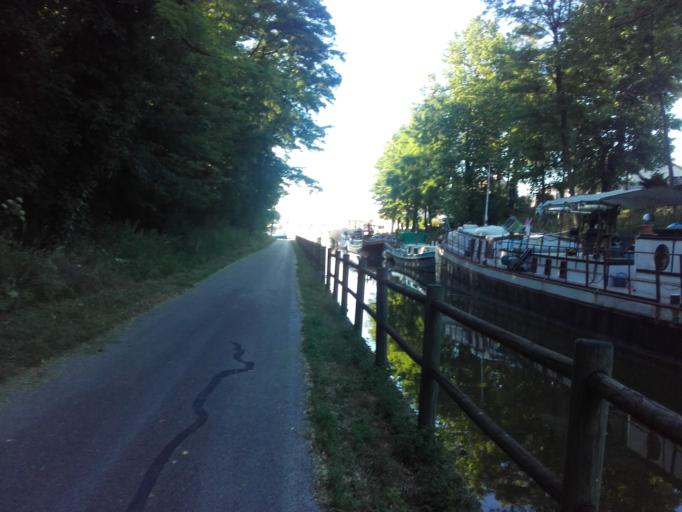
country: FR
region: Bourgogne
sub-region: Departement de Saone-et-Loire
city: Chagny
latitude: 46.9009
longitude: 4.7538
